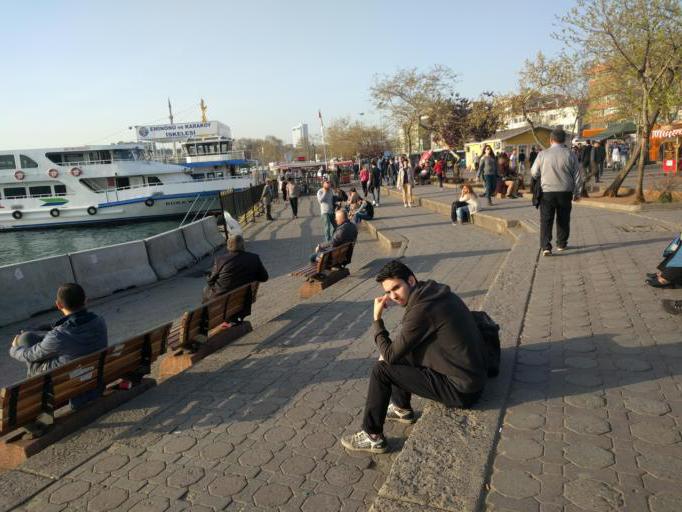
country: TR
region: Istanbul
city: UEskuedar
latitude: 40.9933
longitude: 29.0241
